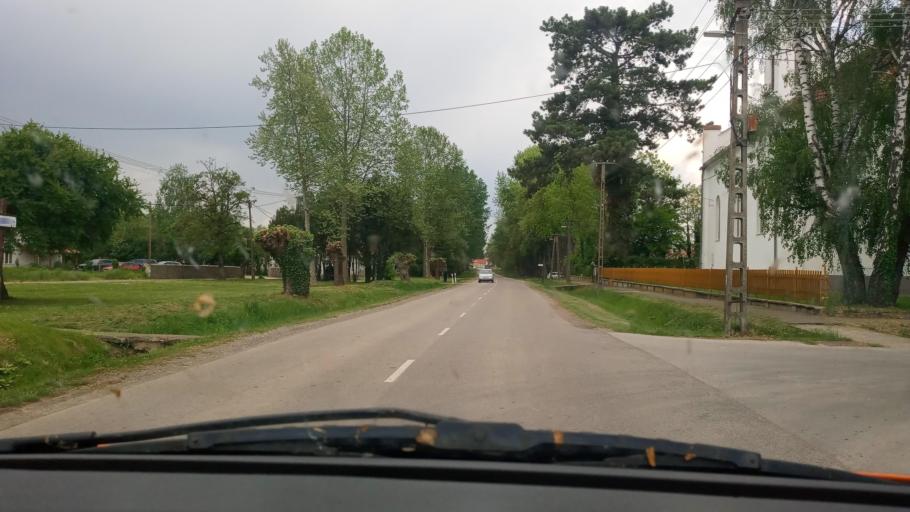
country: HU
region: Baranya
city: Villany
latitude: 45.8419
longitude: 18.4918
